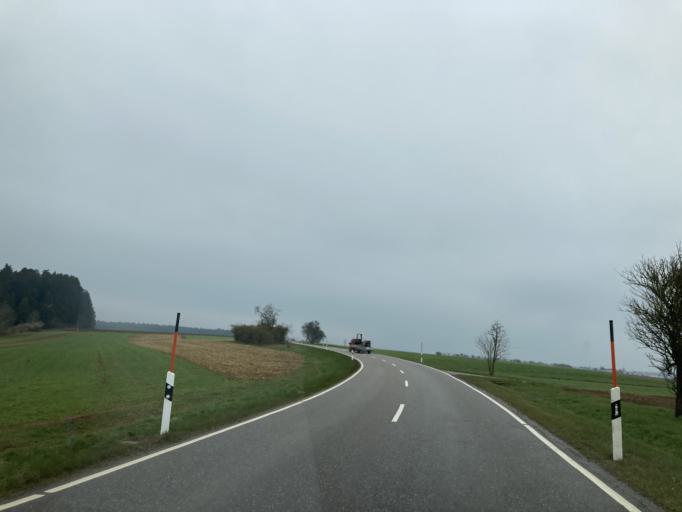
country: DE
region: Baden-Wuerttemberg
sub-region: Freiburg Region
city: Dornhan
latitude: 48.3448
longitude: 8.4736
